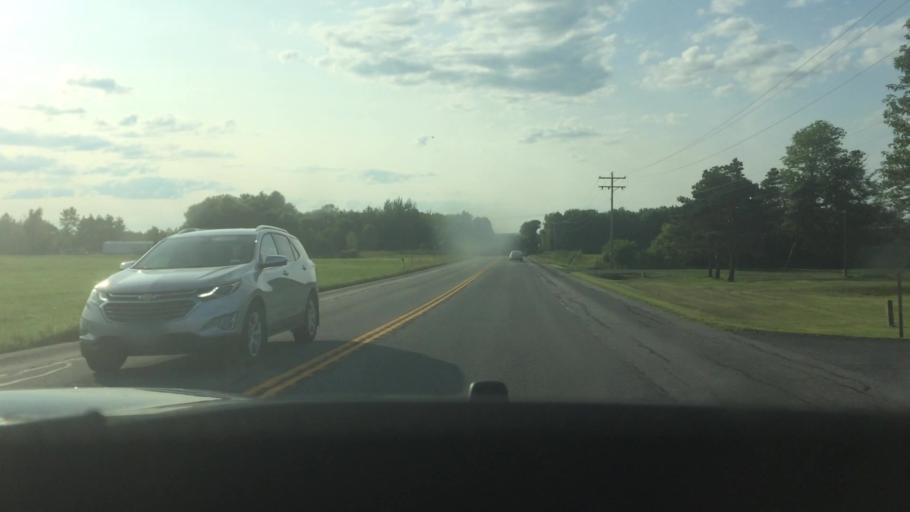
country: US
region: New York
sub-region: St. Lawrence County
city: Canton
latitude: 44.6029
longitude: -75.2010
